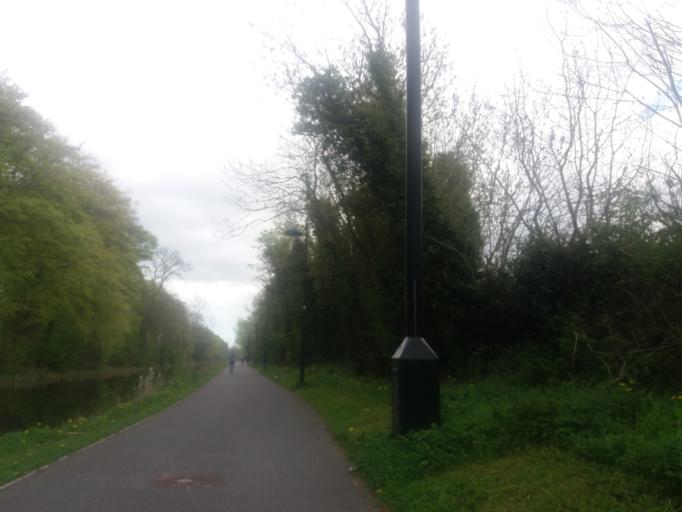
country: IE
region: Leinster
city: Castleknock
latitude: 53.3783
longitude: -6.3468
